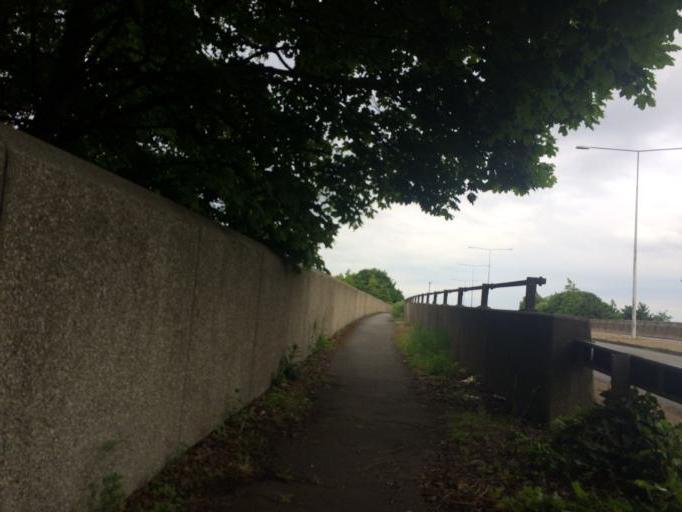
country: GB
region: England
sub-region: Milton Keynes
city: Loughton
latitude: 52.0302
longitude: -0.7715
